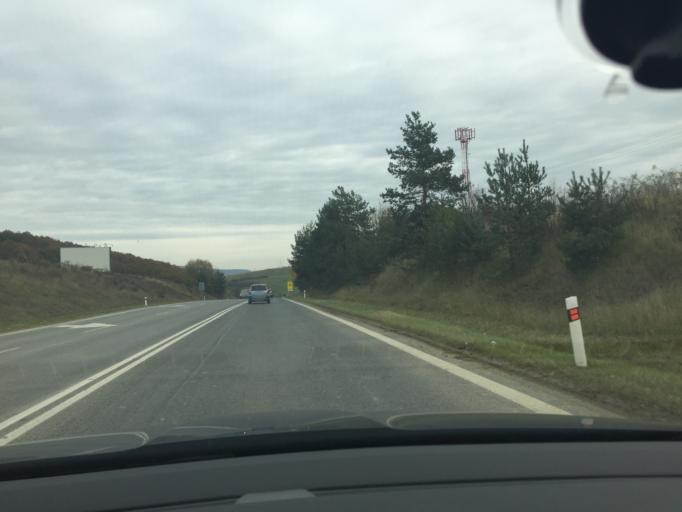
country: SK
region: Presovsky
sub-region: Okres Presov
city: Presov
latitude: 49.0015
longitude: 21.1926
